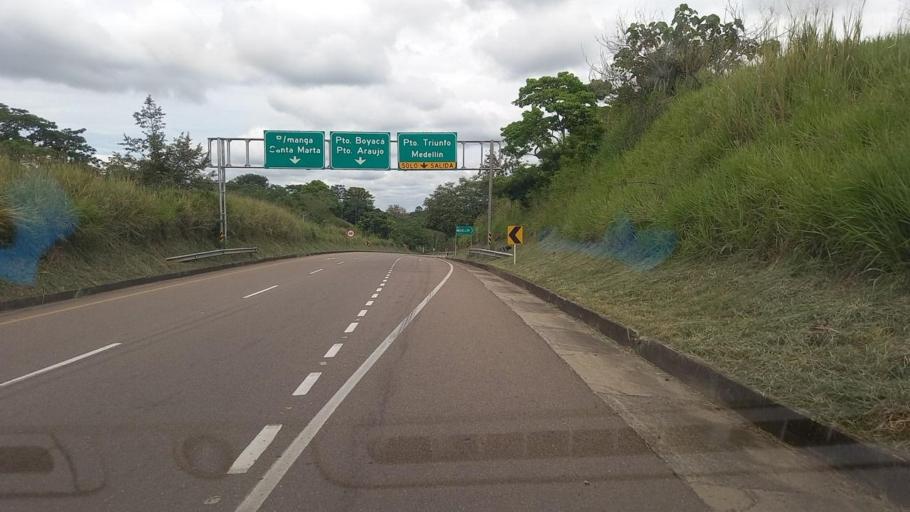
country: CO
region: Antioquia
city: Puerto Triunfo
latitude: 5.8370
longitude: -74.5781
